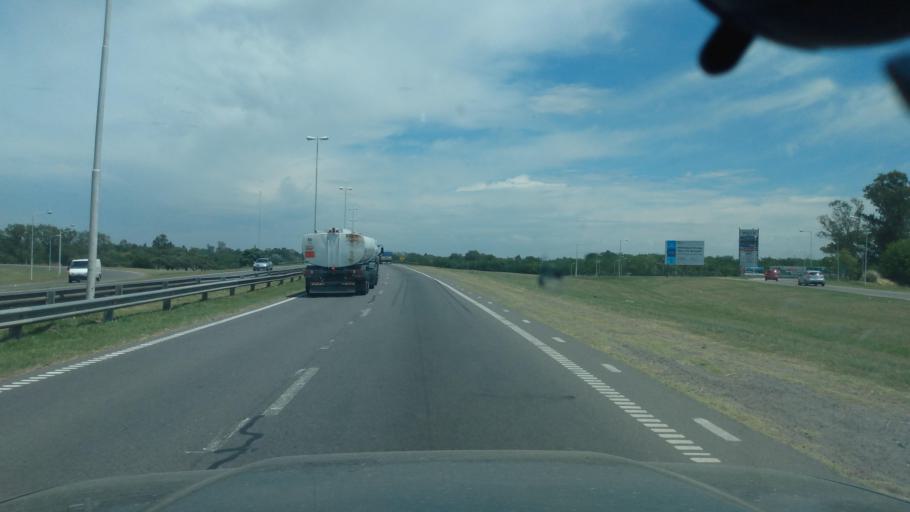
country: AR
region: Buenos Aires
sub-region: Partido de Lujan
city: Lujan
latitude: -34.5507
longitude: -59.1117
